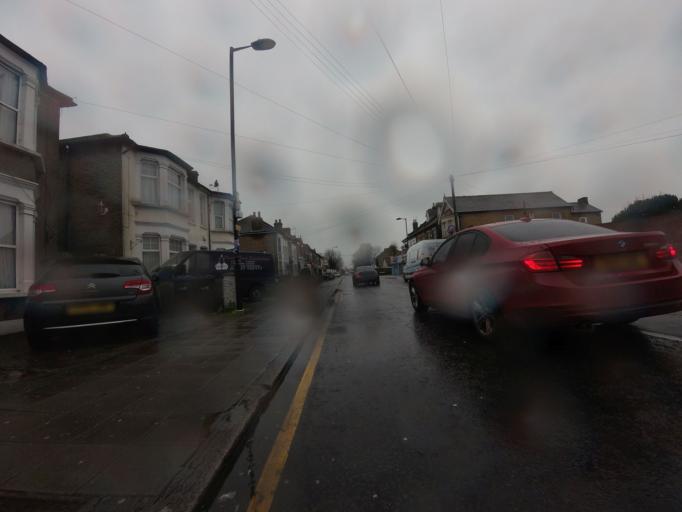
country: GB
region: England
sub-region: Hertfordshire
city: Waltham Cross
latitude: 51.6712
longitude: -0.0291
